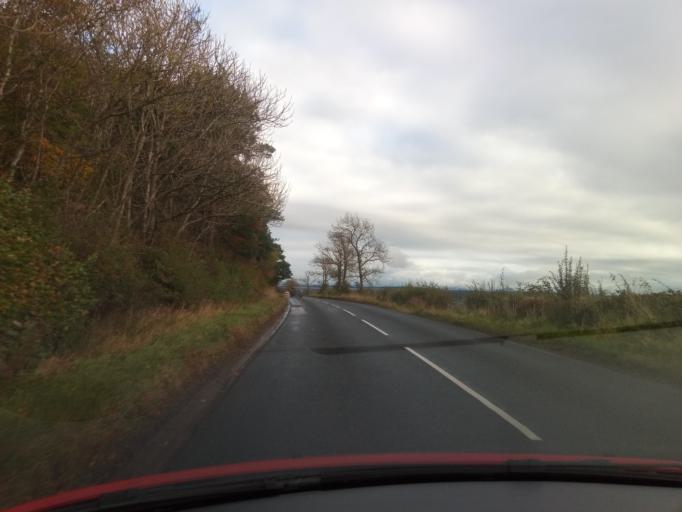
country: GB
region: Scotland
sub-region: The Scottish Borders
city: Newtown St Boswells
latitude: 55.5619
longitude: -2.6982
